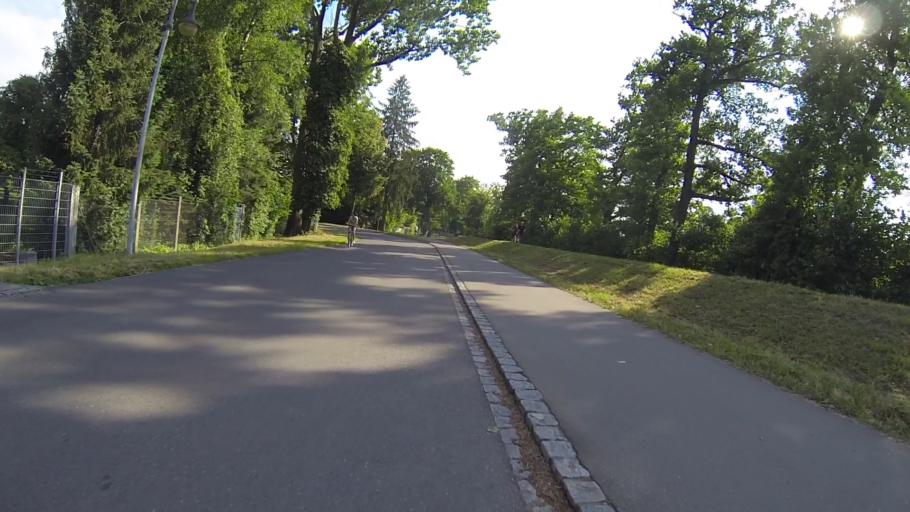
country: DE
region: Bavaria
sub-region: Swabia
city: Neu-Ulm
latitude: 48.4054
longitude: 10.0168
